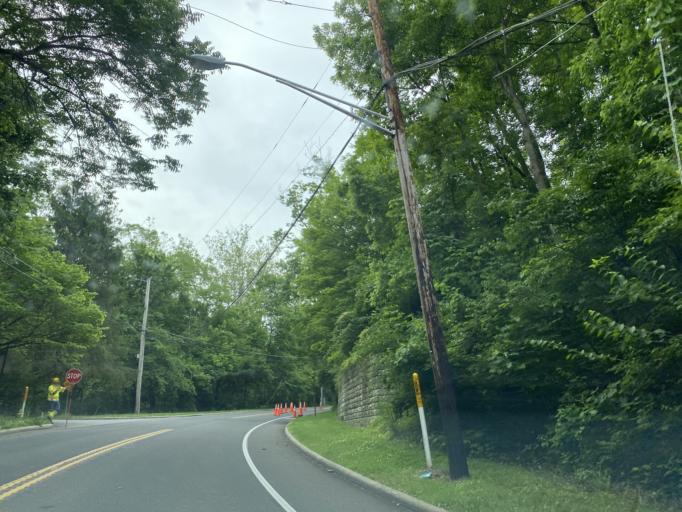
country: US
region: Ohio
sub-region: Hamilton County
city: Salem Heights
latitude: 39.0855
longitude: -84.4108
